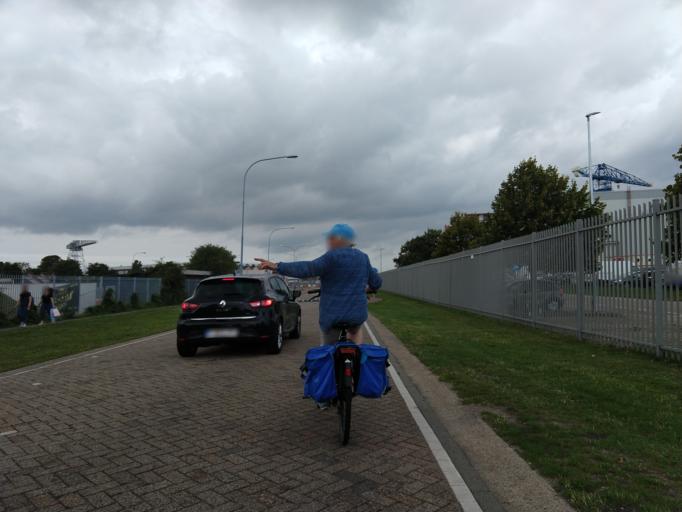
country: NL
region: Zeeland
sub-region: Gemeente Vlissingen
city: Vlissingen
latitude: 51.4423
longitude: 3.5824
